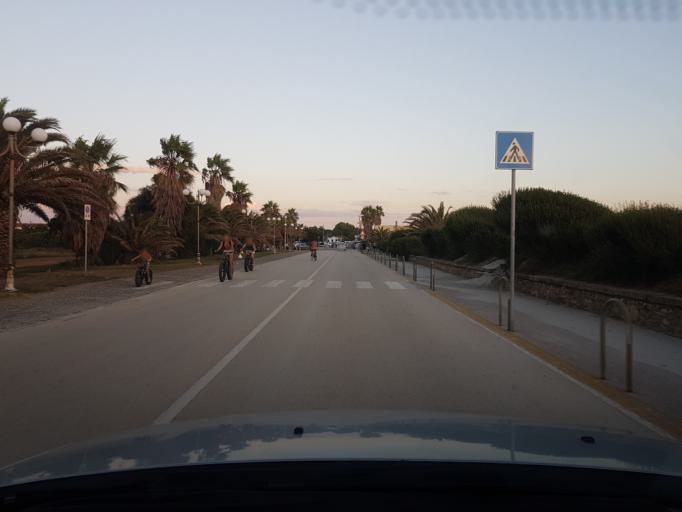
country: IT
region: Sardinia
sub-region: Provincia di Oristano
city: Riola Sardo
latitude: 40.0294
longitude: 8.4068
